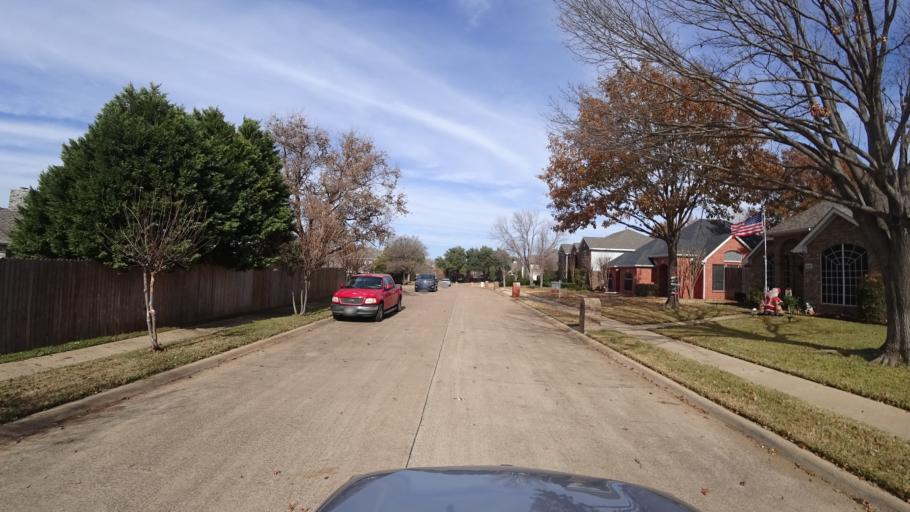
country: US
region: Texas
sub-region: Denton County
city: Highland Village
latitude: 33.0774
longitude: -97.0346
